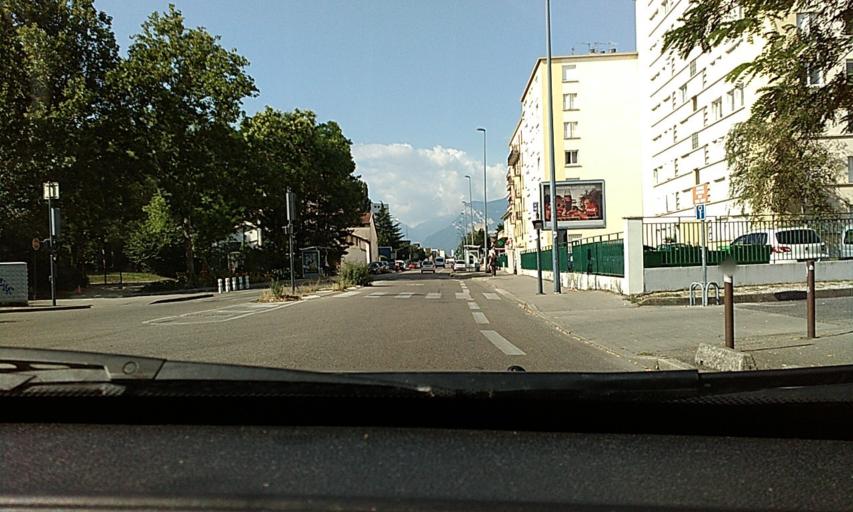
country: FR
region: Rhone-Alpes
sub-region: Departement de l'Isere
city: Grenoble
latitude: 45.1700
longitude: 5.7230
